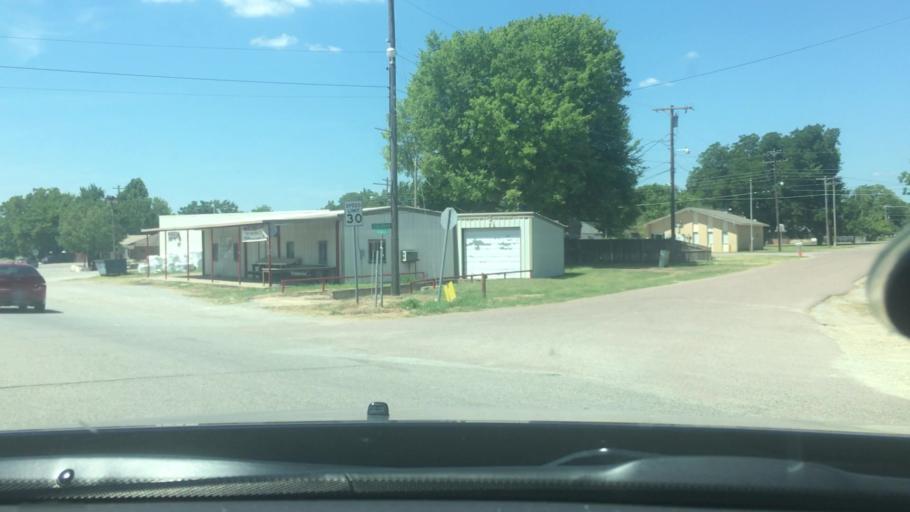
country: US
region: Oklahoma
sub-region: Bryan County
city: Colbert
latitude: 33.8545
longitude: -96.5016
